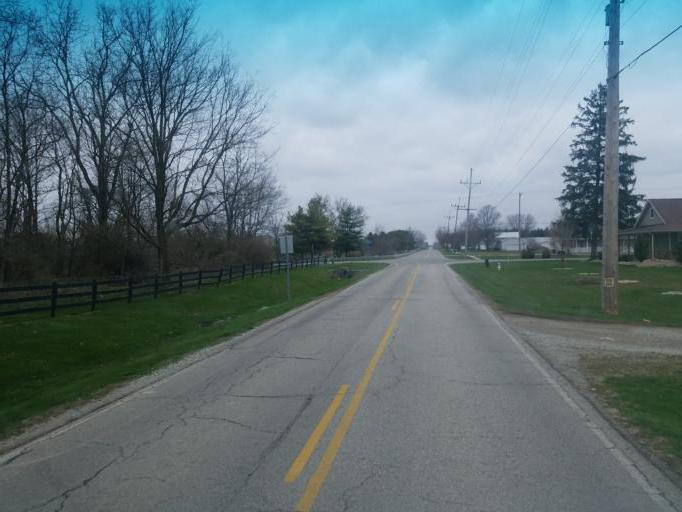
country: US
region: Ohio
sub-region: Marion County
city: Marion
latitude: 40.5195
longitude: -83.1509
